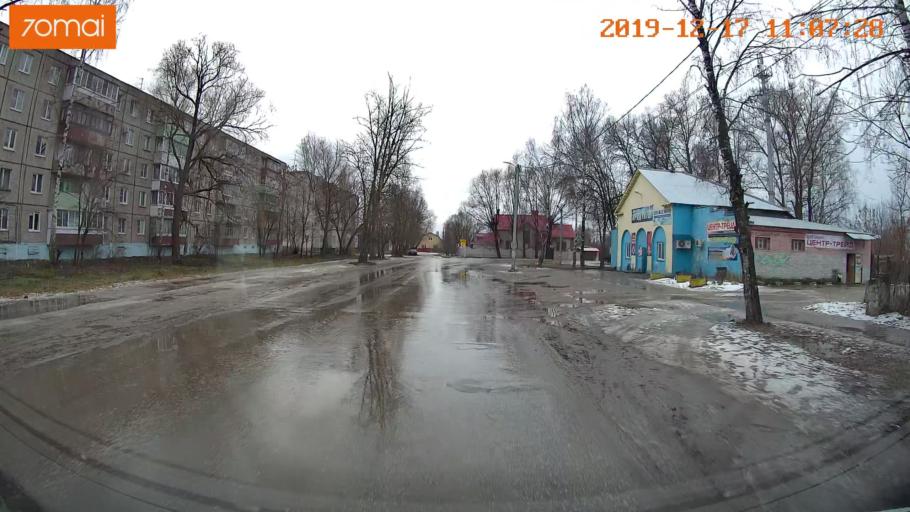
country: RU
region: Vladimir
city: Gus'-Khrustal'nyy
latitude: 55.6105
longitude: 40.6446
